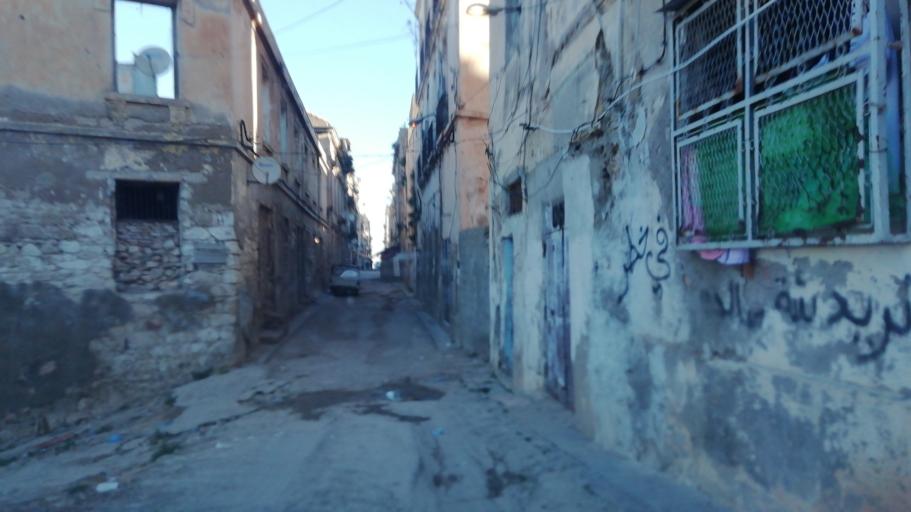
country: DZ
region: Oran
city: Oran
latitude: 35.7005
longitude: -0.6524
